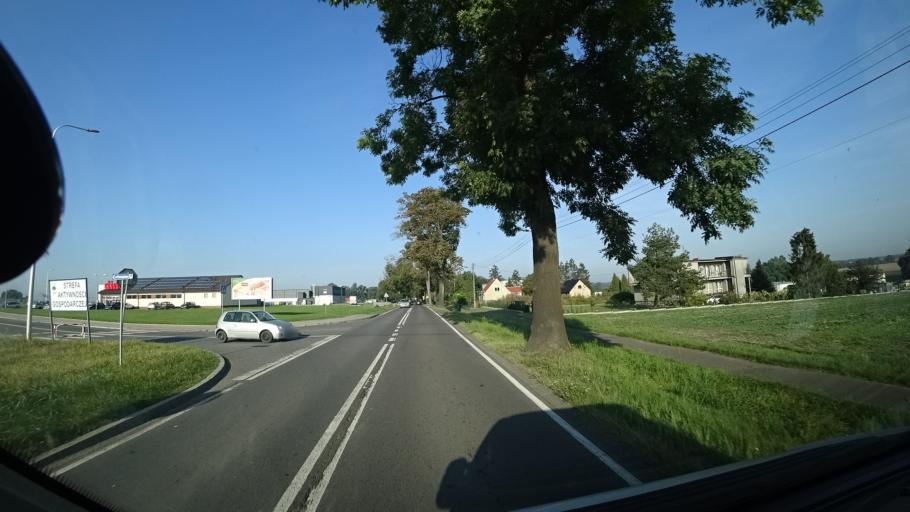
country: PL
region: Silesian Voivodeship
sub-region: Powiat gliwicki
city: Sosnicowice
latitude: 50.2695
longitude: 18.5438
